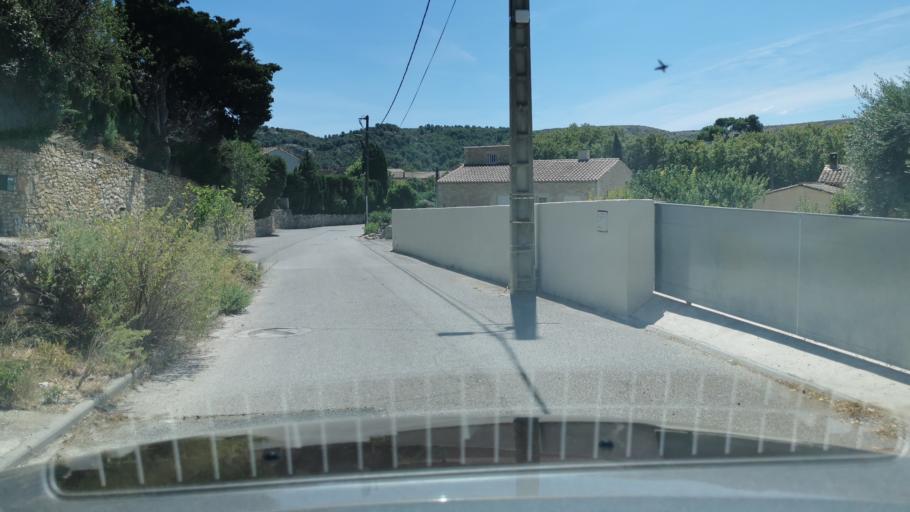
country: FR
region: Languedoc-Roussillon
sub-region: Departement de l'Aude
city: Armissan
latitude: 43.1895
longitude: 3.0941
